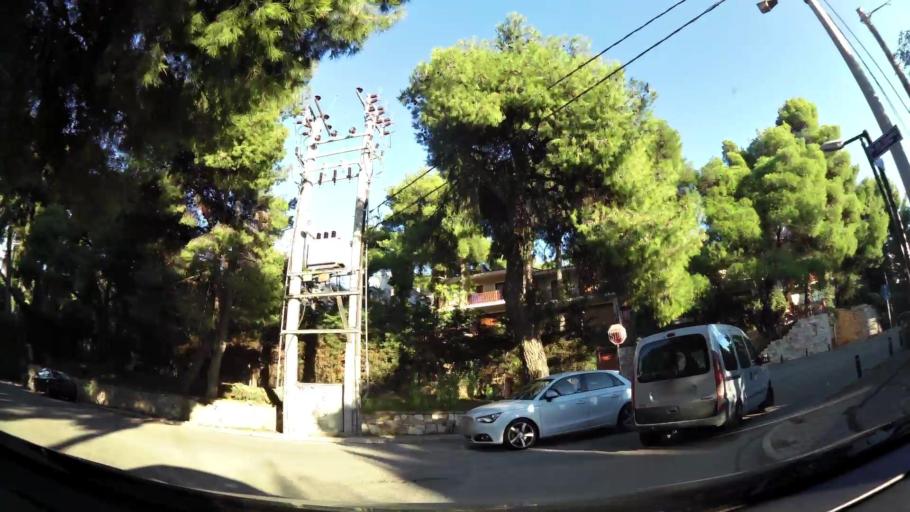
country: GR
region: Attica
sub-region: Nomarchia Athinas
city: Nea Erythraia
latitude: 38.0938
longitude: 23.8255
